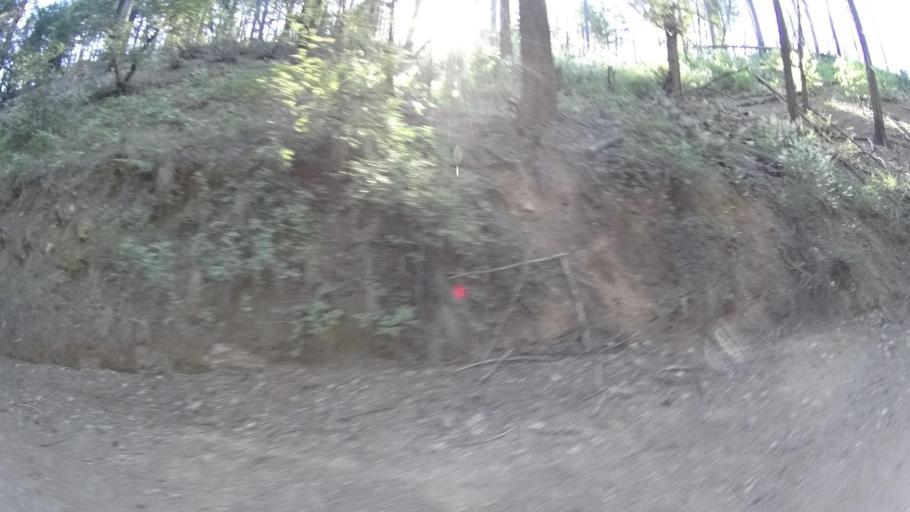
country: US
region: California
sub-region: Lake County
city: Upper Lake
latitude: 39.3760
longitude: -122.9906
